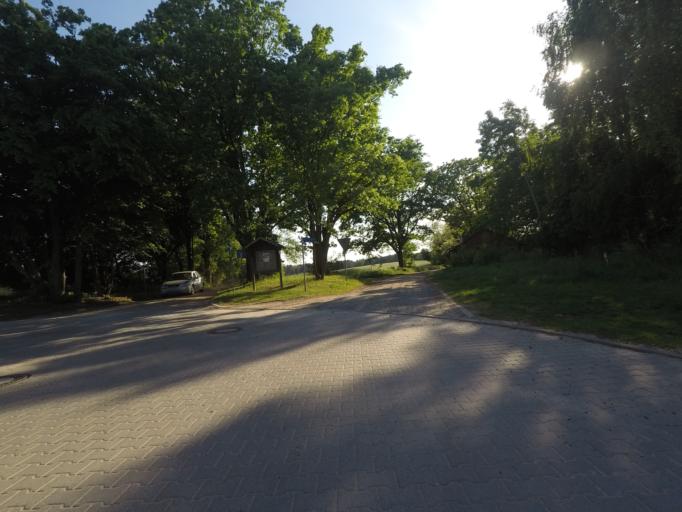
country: DE
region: Brandenburg
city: Joachimsthal
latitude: 52.8886
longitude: 13.6989
